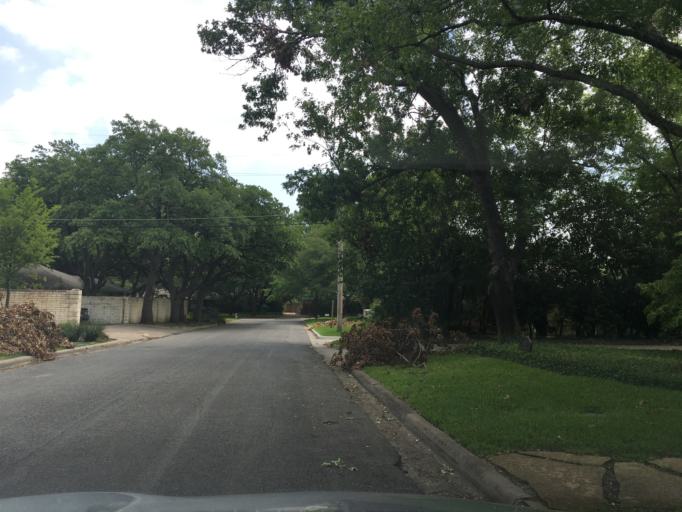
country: US
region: Texas
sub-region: Dallas County
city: University Park
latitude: 32.9047
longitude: -96.8014
